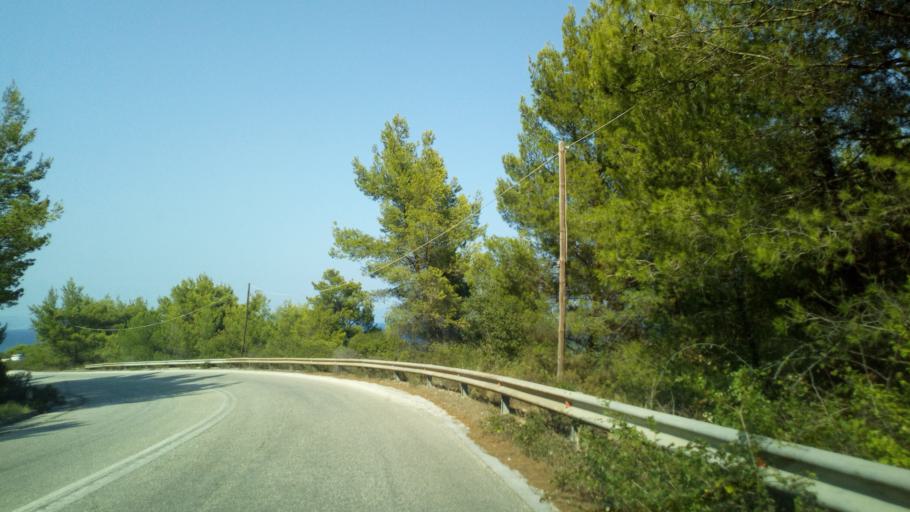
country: GR
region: Central Macedonia
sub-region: Nomos Chalkidikis
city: Sarti
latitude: 40.1147
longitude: 23.9778
